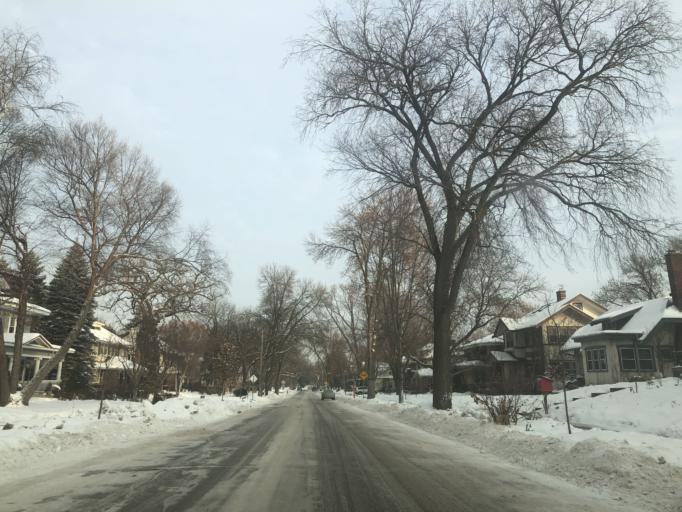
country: US
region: Minnesota
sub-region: Hennepin County
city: Richfield
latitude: 44.9165
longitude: -93.2935
